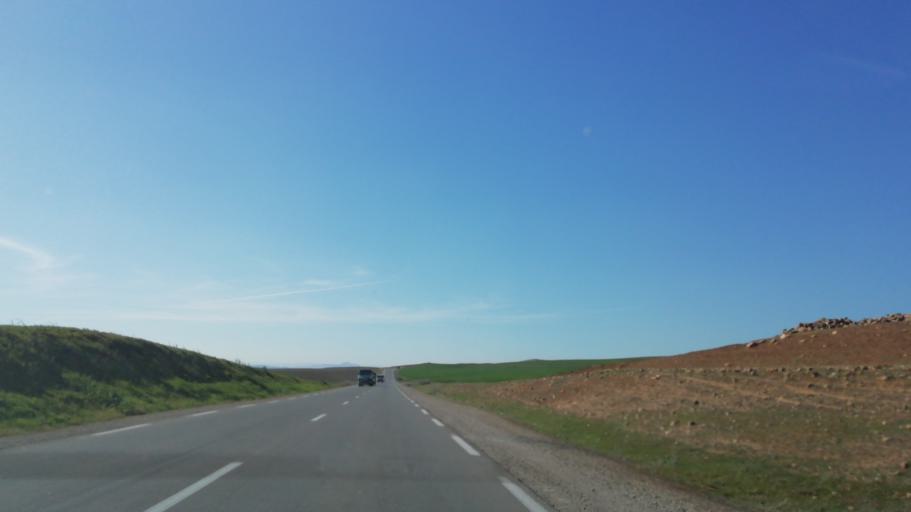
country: DZ
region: Mascara
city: Oued el Abtal
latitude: 35.4456
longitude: 0.8230
